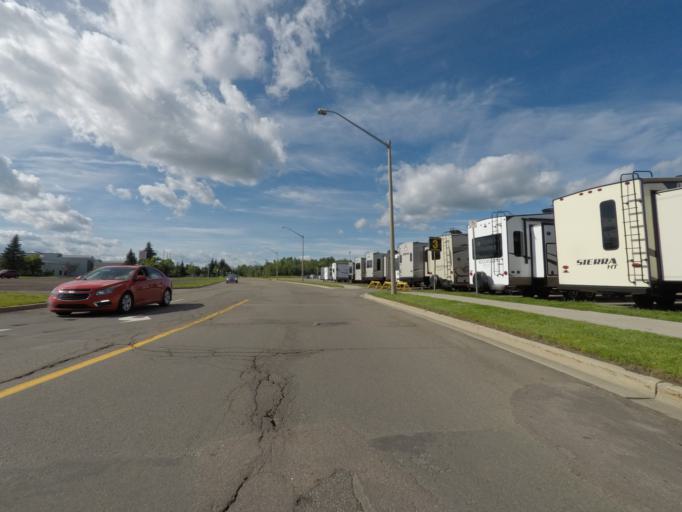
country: CA
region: New Brunswick
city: Moncton
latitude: 46.0949
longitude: -64.8326
